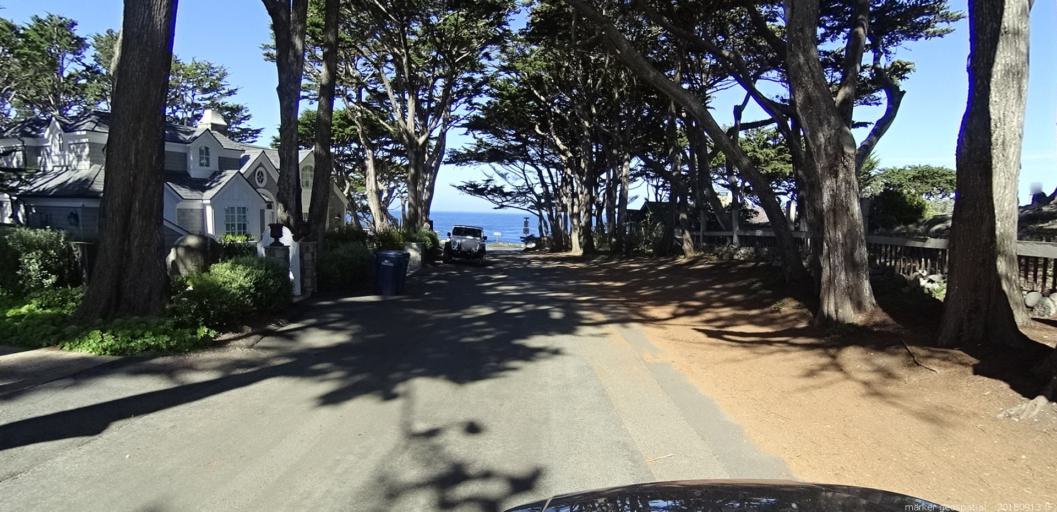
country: US
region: California
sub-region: Monterey County
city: Carmel-by-the-Sea
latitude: 36.5436
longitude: -121.9326
